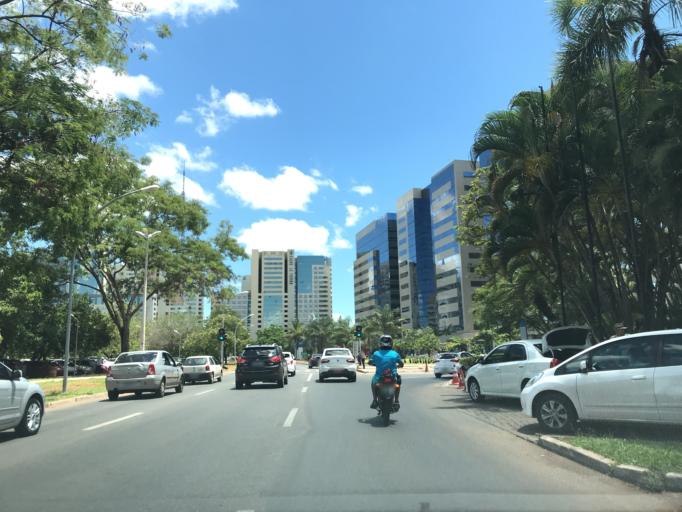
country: BR
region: Federal District
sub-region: Brasilia
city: Brasilia
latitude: -15.7964
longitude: -47.8948
